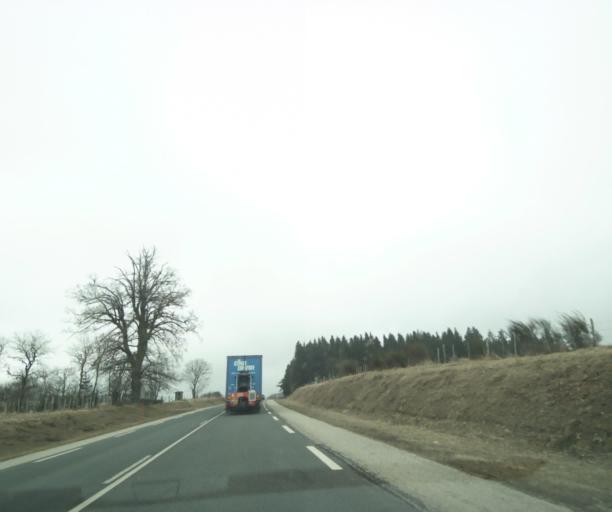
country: FR
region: Languedoc-Roussillon
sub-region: Departement de la Lozere
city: Langogne
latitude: 44.7052
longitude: 3.8201
